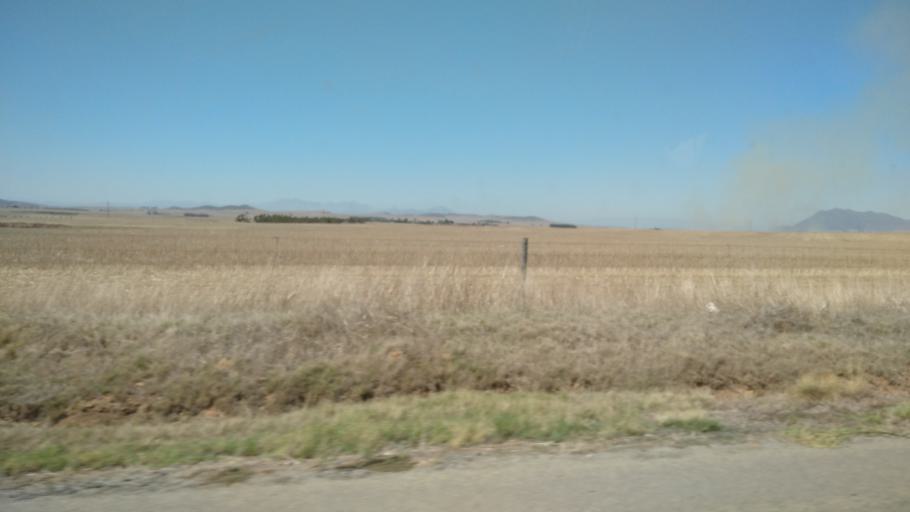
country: ZA
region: Western Cape
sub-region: West Coast District Municipality
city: Moorreesburg
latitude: -33.2887
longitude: 18.6075
